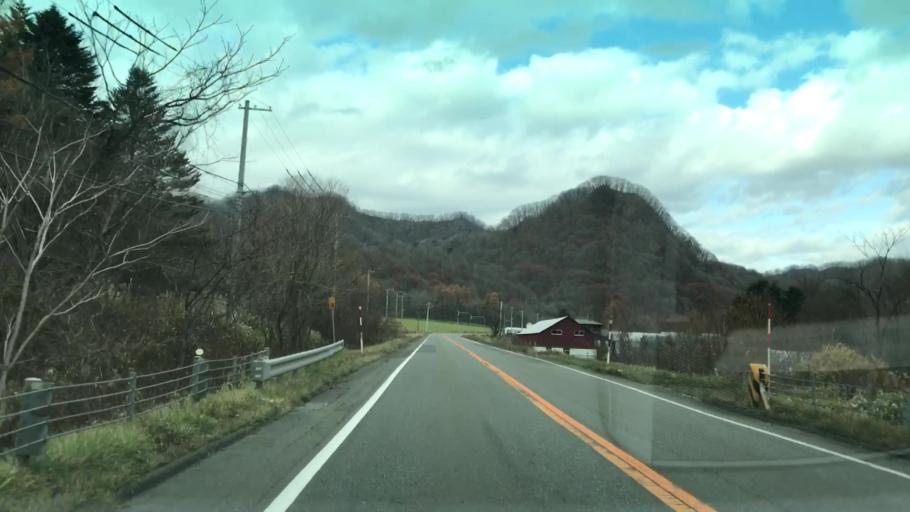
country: JP
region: Hokkaido
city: Shizunai-furukawacho
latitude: 42.8019
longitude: 142.3978
